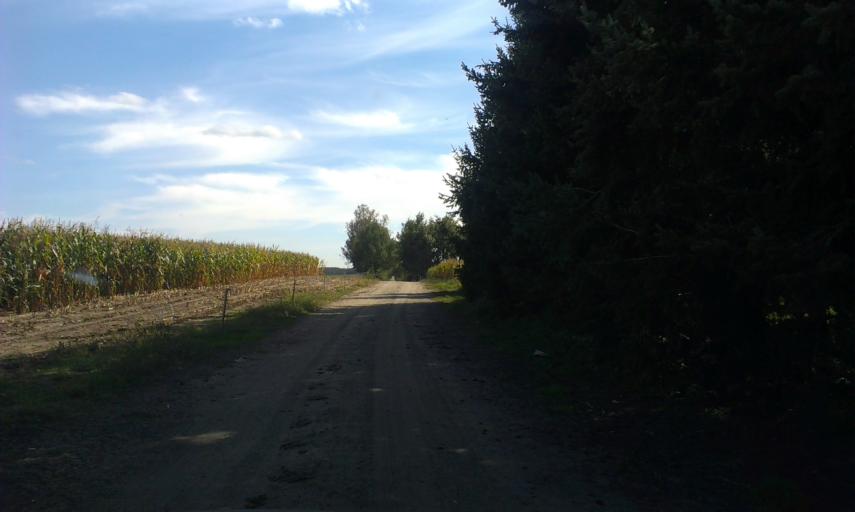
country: PL
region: Greater Poland Voivodeship
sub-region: Powiat pilski
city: Lobzenica
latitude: 53.2964
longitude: 17.1508
